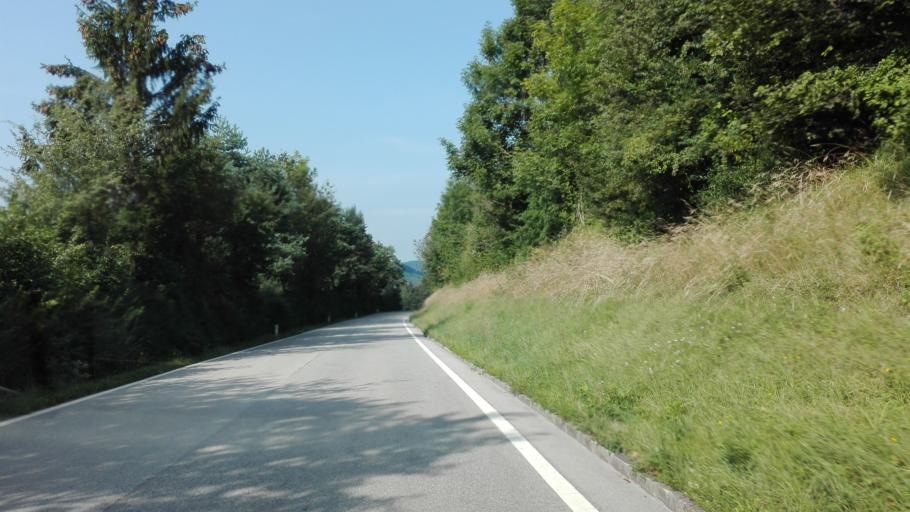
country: AT
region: Lower Austria
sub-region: Politischer Bezirk Sankt Polten
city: Rabenstein an der Pielach
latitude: 48.0366
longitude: 15.4984
